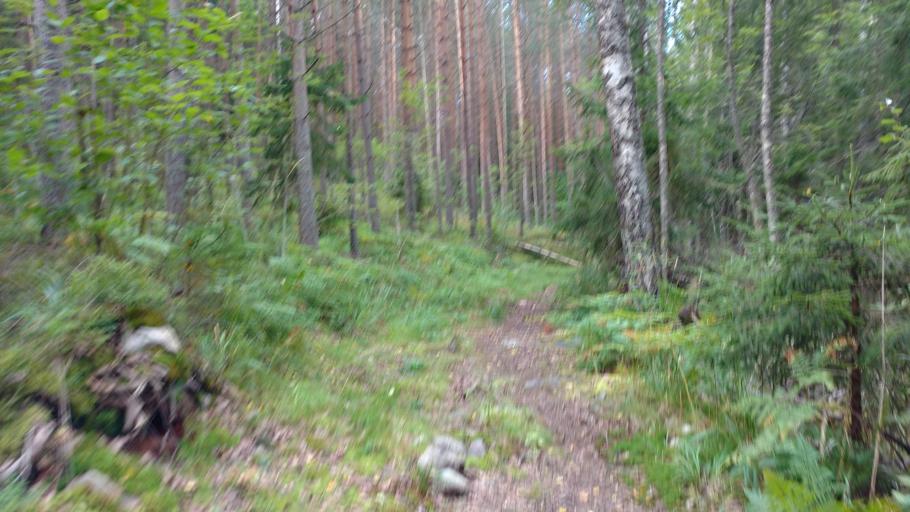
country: FI
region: Varsinais-Suomi
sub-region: Salo
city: Salo
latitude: 60.3627
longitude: 23.1716
